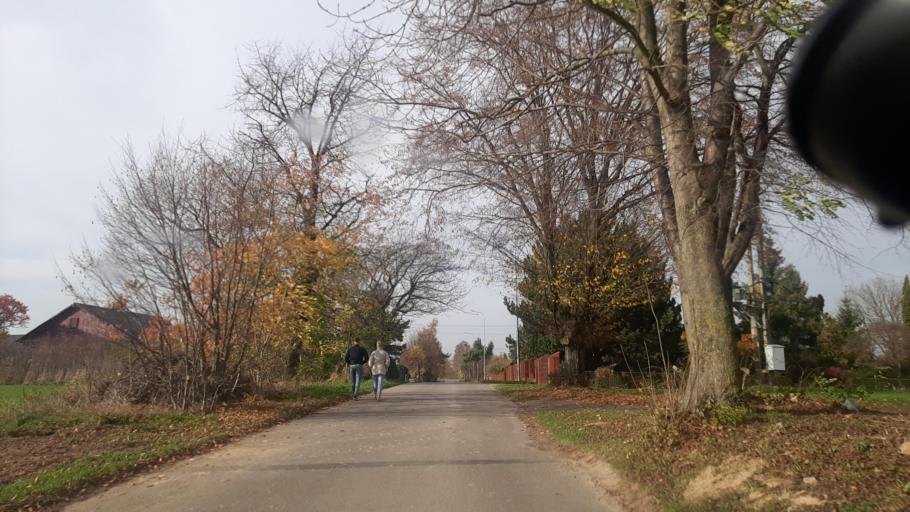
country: PL
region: Lublin Voivodeship
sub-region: Powiat lubelski
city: Jastkow
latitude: 51.3373
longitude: 22.4269
